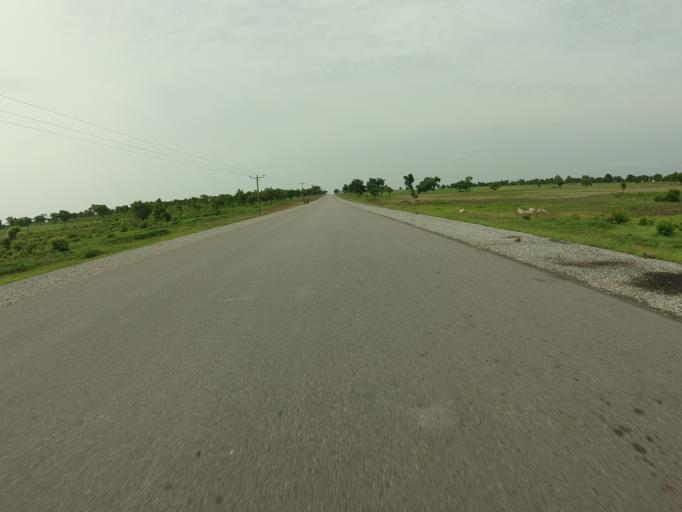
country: GH
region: Northern
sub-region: Yendi
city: Yendi
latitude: 9.8179
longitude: -0.1175
